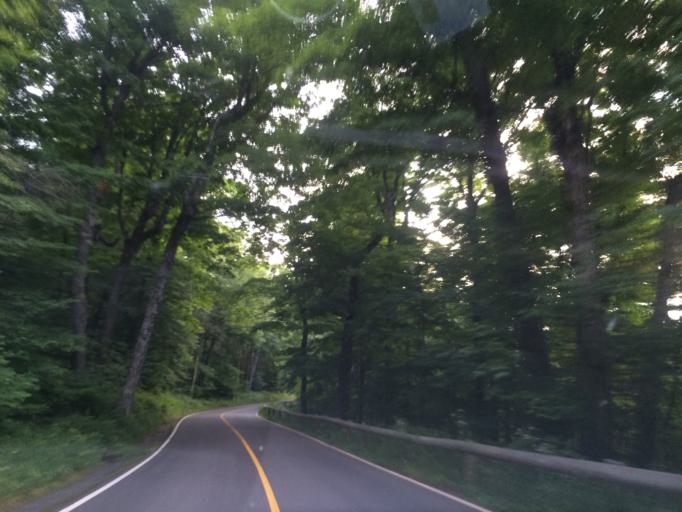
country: US
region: Massachusetts
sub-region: Berkshire County
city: Adams
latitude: 42.6233
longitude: -73.1949
